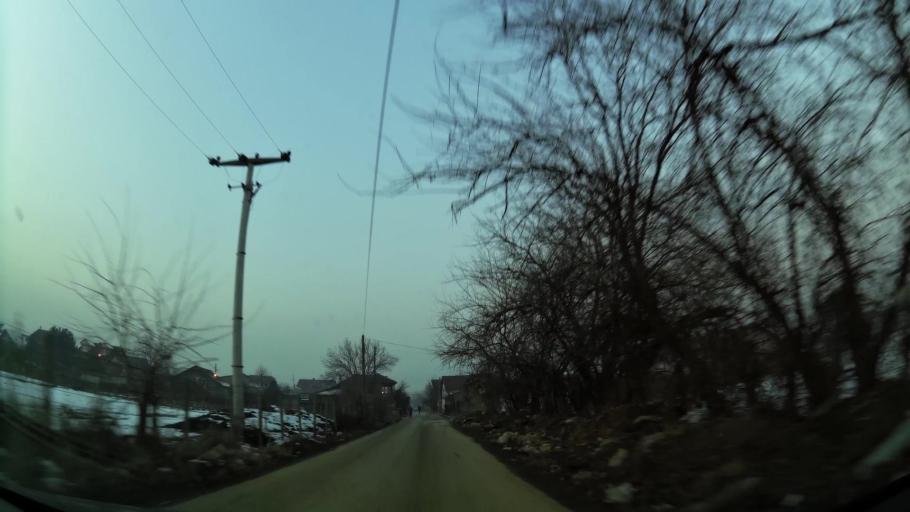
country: MK
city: Creshevo
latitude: 42.0099
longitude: 21.5171
